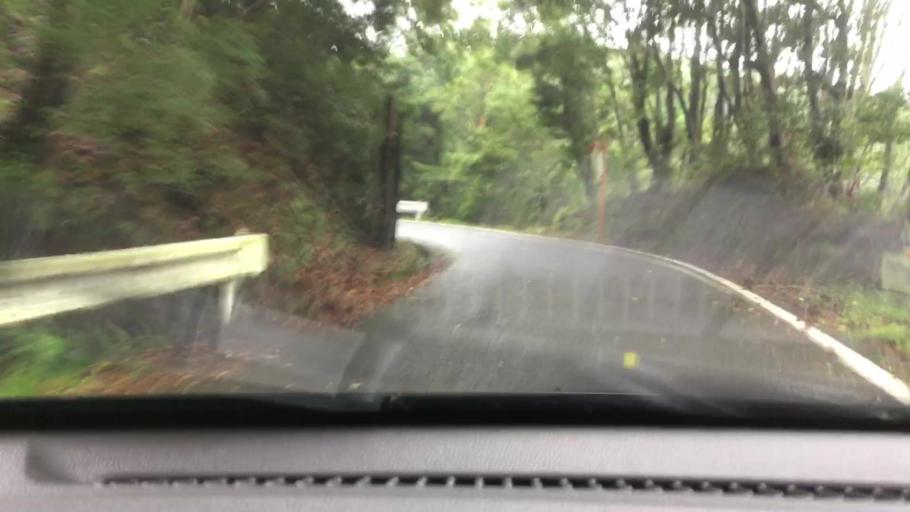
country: JP
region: Nagasaki
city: Togitsu
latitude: 32.9176
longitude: 129.7265
